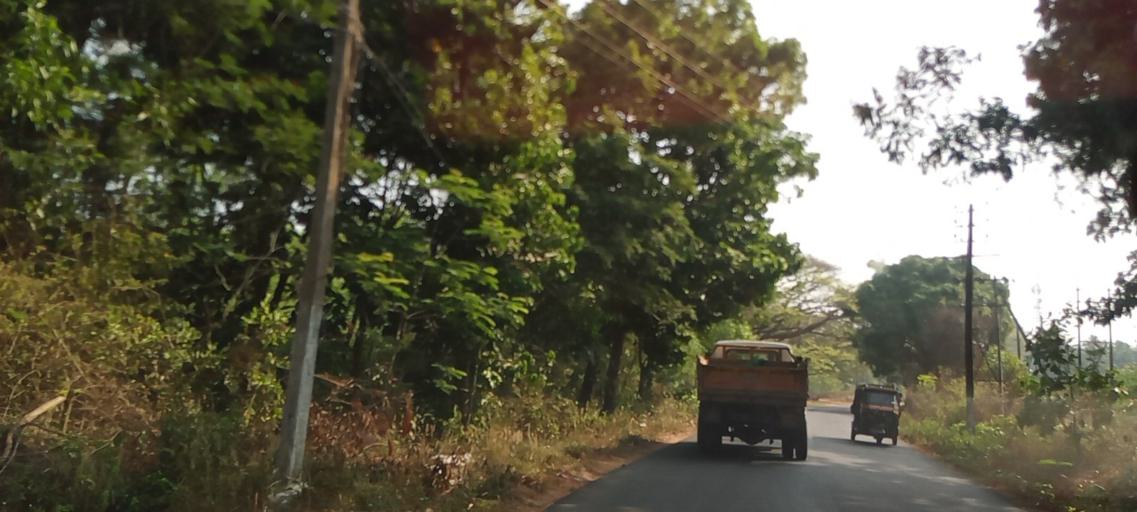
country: IN
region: Karnataka
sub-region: Udupi
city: Coondapoor
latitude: 13.5156
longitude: 74.7429
